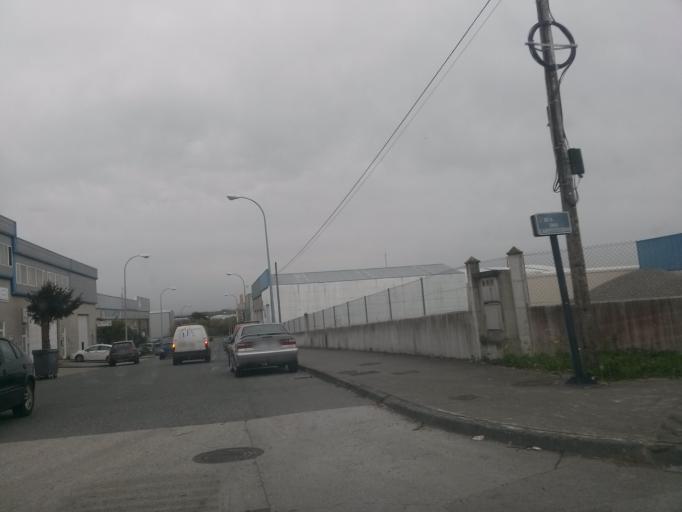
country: ES
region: Galicia
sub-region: Provincia de Lugo
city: Lugo
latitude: 43.0429
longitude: -7.5623
